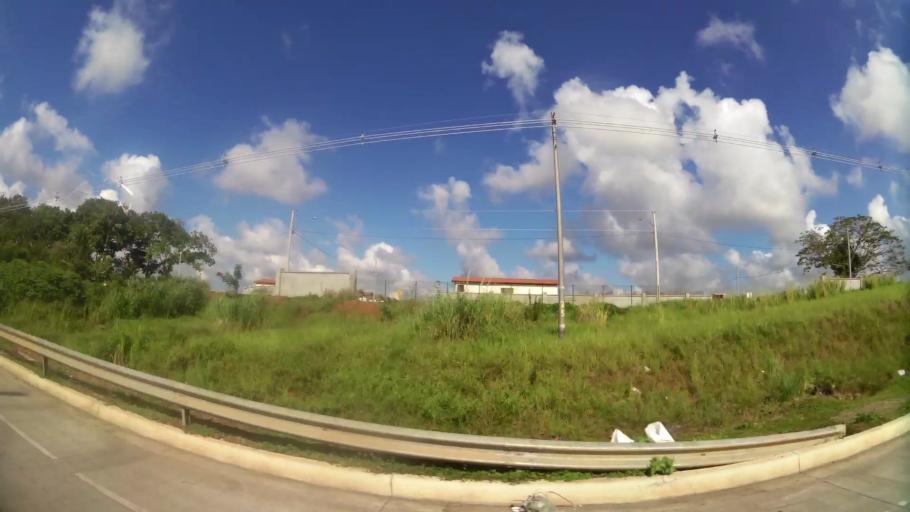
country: PA
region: Panama
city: Nuevo Arraijan
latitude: 8.8948
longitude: -79.7468
